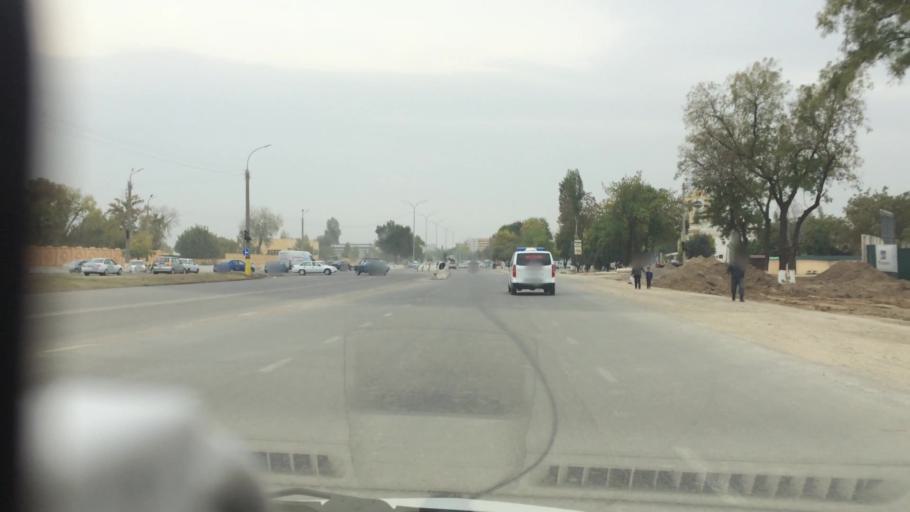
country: UZ
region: Toshkent
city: Salor
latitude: 41.3046
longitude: 69.3412
